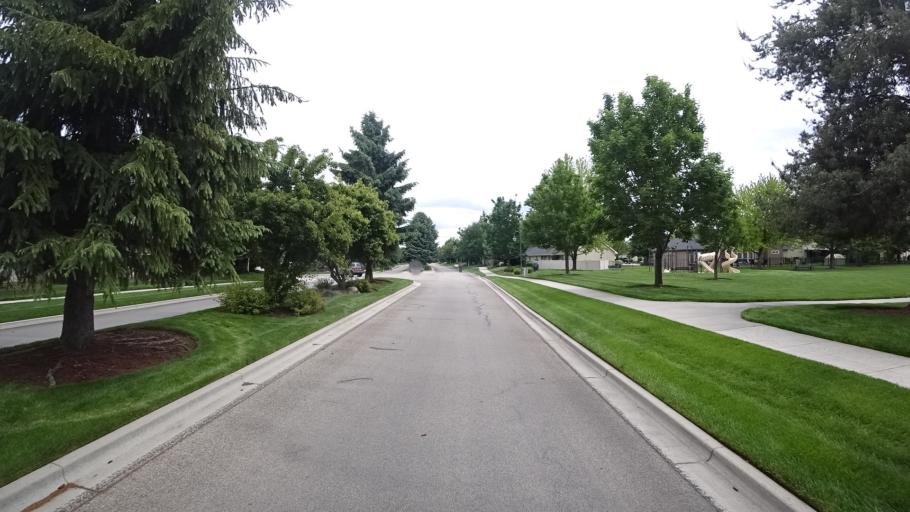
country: US
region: Idaho
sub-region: Ada County
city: Meridian
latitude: 43.6431
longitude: -116.4117
